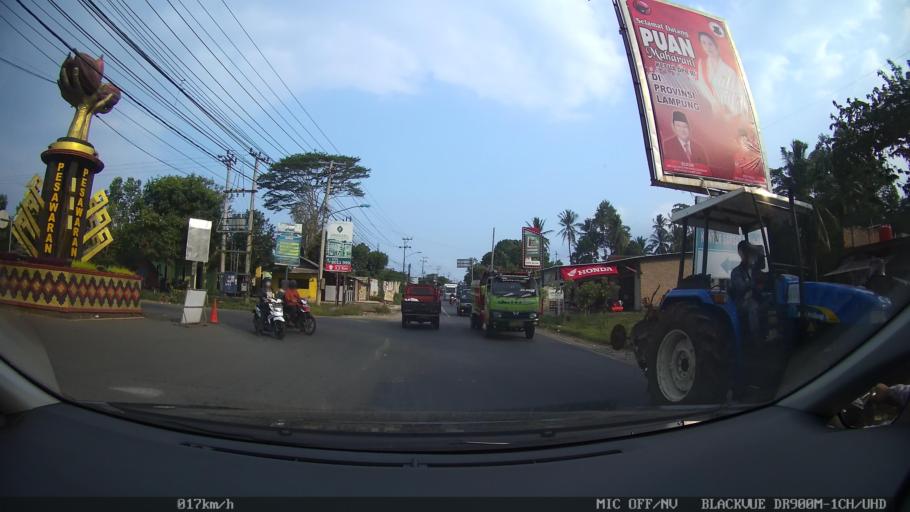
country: ID
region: Lampung
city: Natar
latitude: -5.3694
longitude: 105.1915
